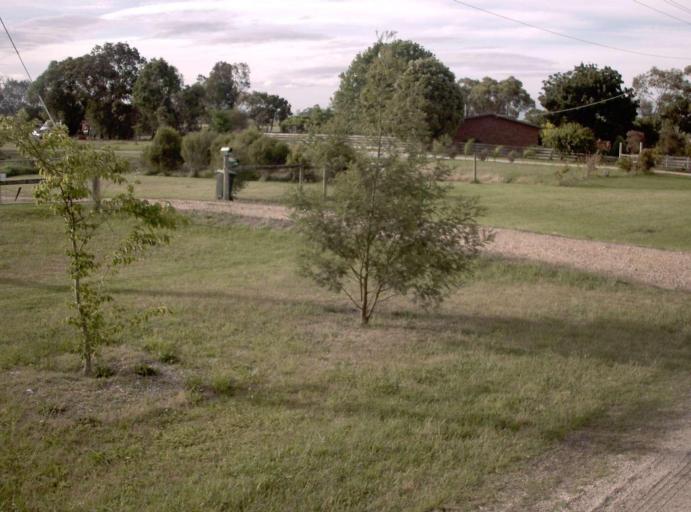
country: AU
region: Victoria
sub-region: Wellington
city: Sale
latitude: -37.9540
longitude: 146.9874
